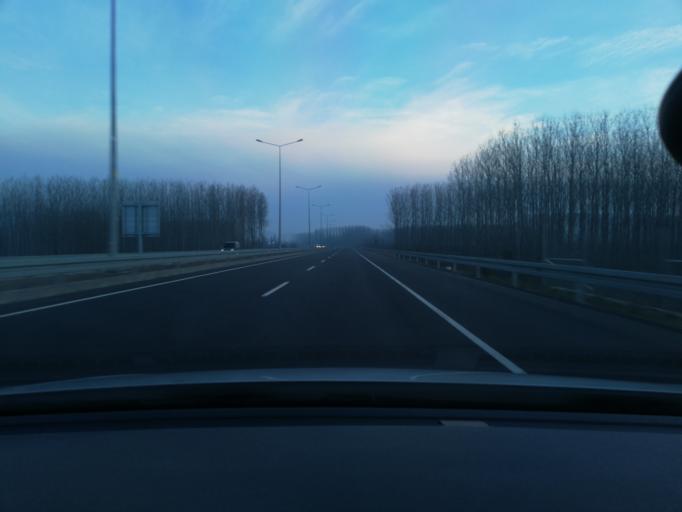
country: TR
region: Duzce
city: Duzce
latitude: 40.8074
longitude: 31.1688
